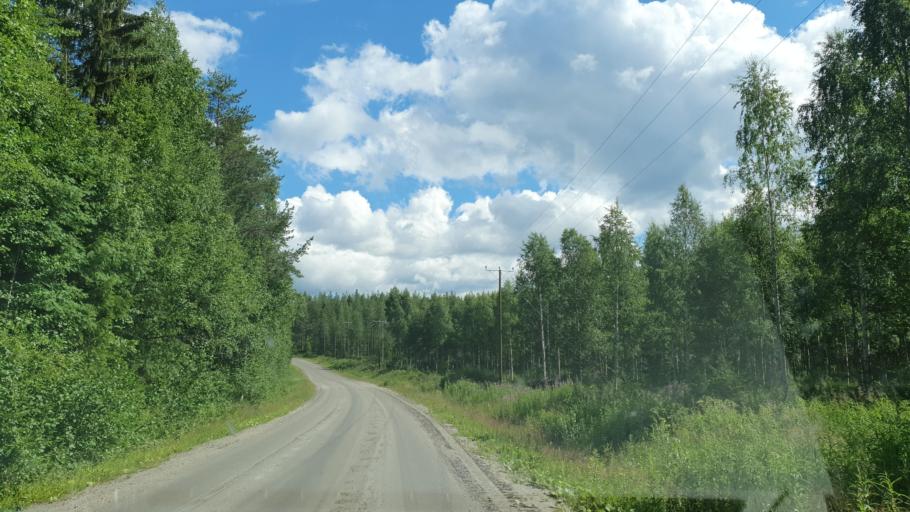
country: FI
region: Kainuu
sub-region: Kehys-Kainuu
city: Kuhmo
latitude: 64.0966
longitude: 29.9135
